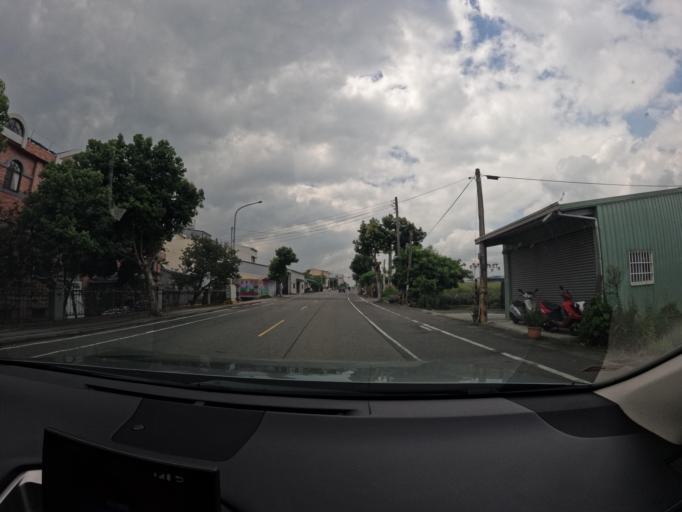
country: TW
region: Taiwan
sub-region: Nantou
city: Nantou
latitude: 23.9133
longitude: 120.6374
